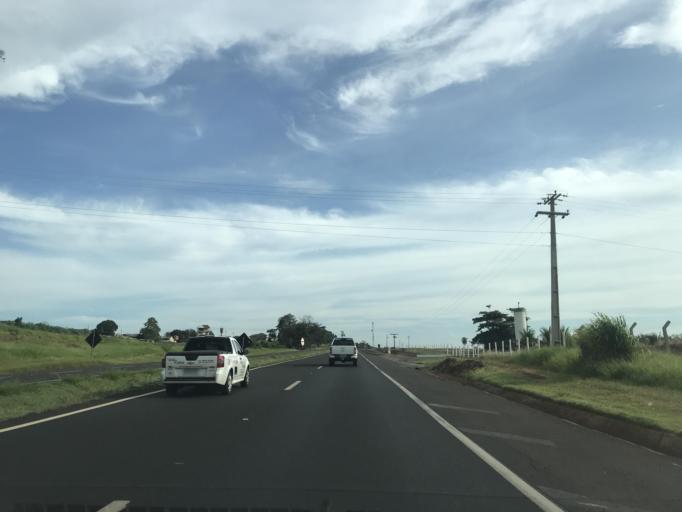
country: BR
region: Parana
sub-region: Mandaguacu
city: Mandaguacu
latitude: -23.3295
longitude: -52.1116
